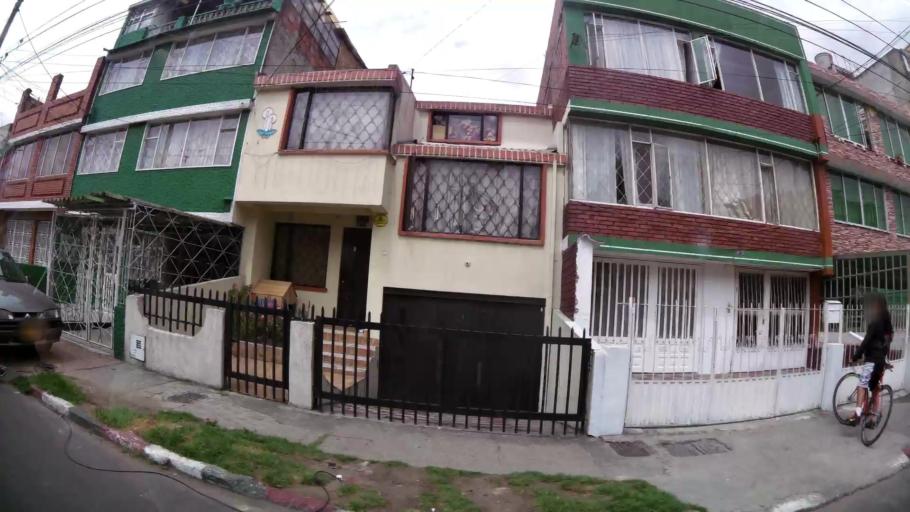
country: CO
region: Bogota D.C.
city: Bogota
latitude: 4.6210
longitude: -74.1086
